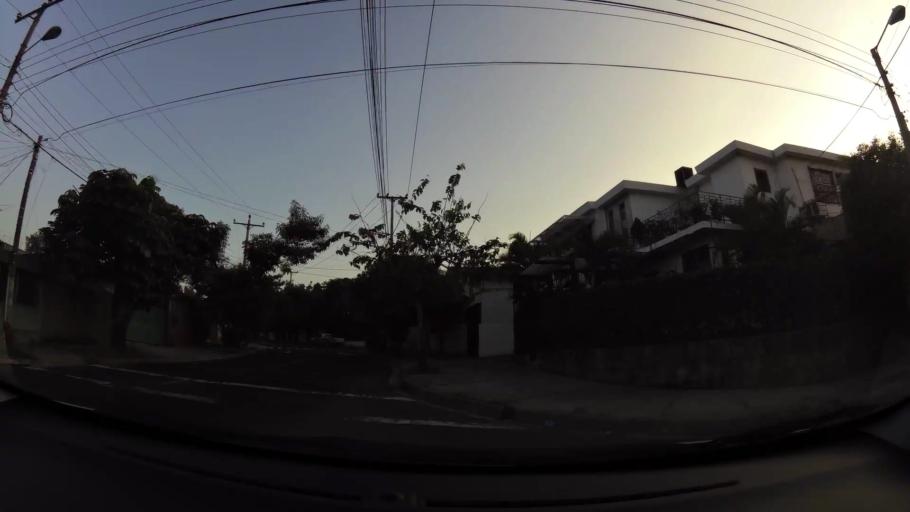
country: SV
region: San Salvador
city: San Salvador
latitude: 13.6812
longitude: -89.2112
